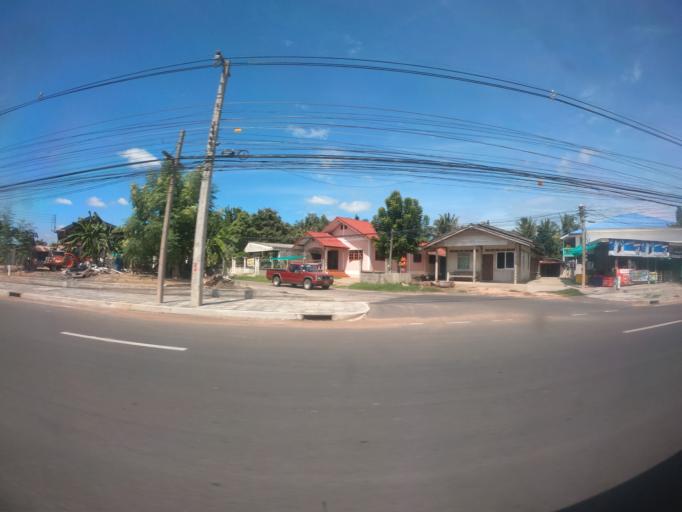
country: TH
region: Surin
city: Prasat
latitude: 14.6191
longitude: 103.4138
